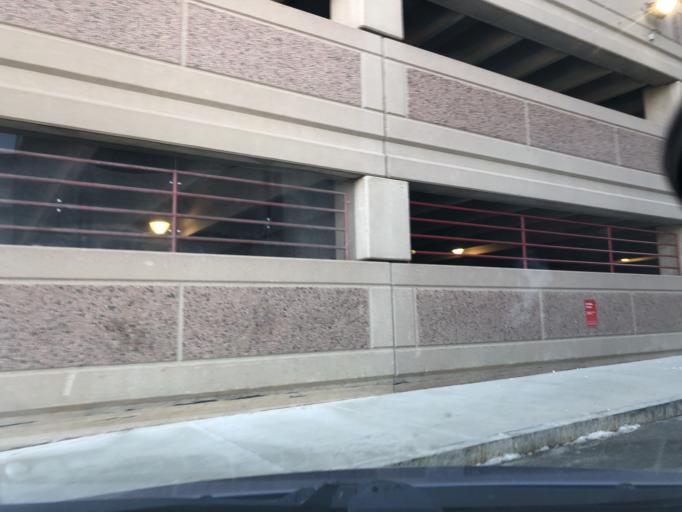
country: US
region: Massachusetts
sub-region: Suffolk County
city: Boston
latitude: 42.3381
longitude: -71.0869
